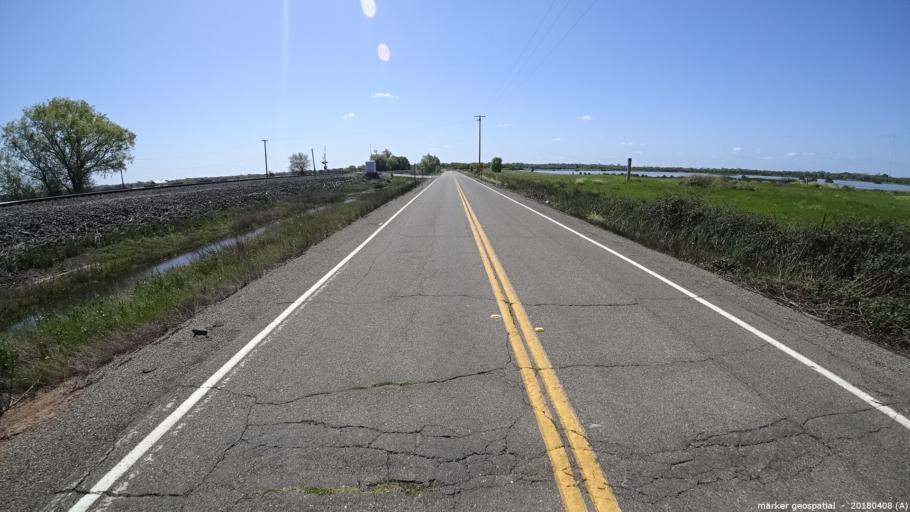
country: US
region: California
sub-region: San Joaquin County
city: Thornton
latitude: 38.2766
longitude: -121.4394
